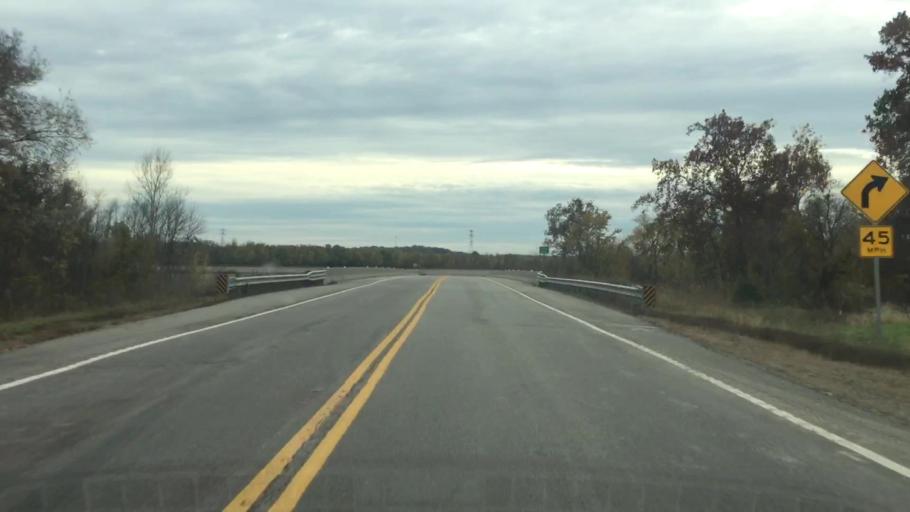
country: US
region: Missouri
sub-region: Callaway County
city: Fulton
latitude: 38.7095
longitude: -91.7425
